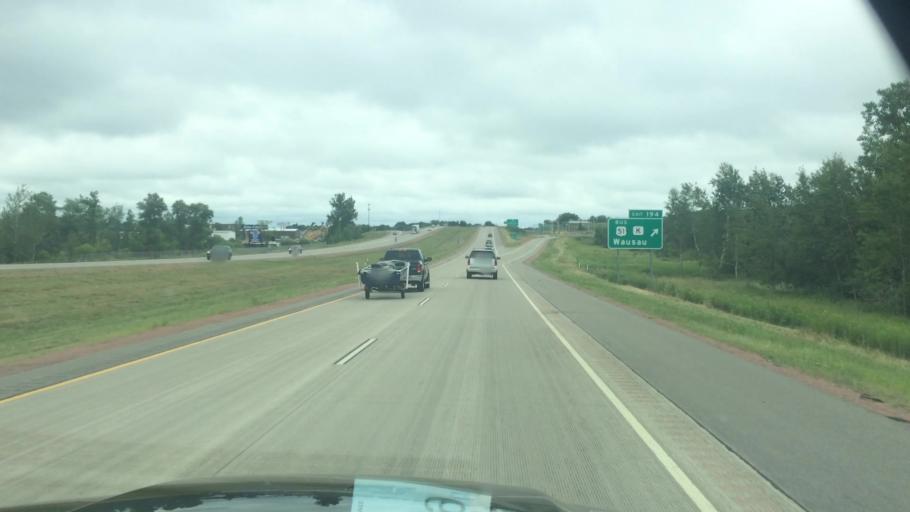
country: US
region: Wisconsin
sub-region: Marathon County
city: Wausau
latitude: 44.9974
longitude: -89.6579
